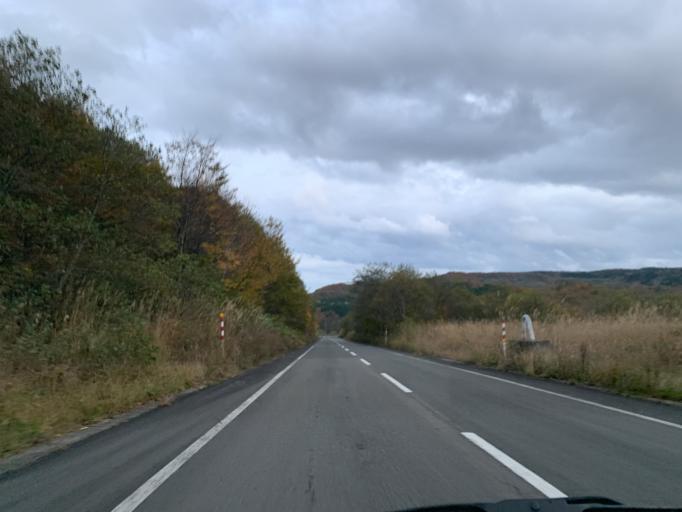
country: JP
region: Iwate
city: Ichinoseki
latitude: 39.0185
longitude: 140.8767
